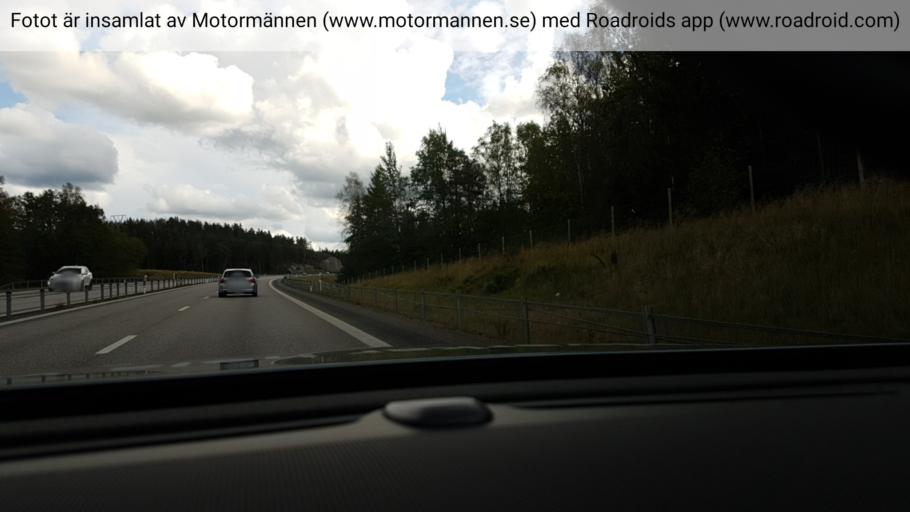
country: SE
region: Vaestra Goetaland
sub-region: Lilla Edets Kommun
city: Lodose
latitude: 58.0659
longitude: 12.1612
